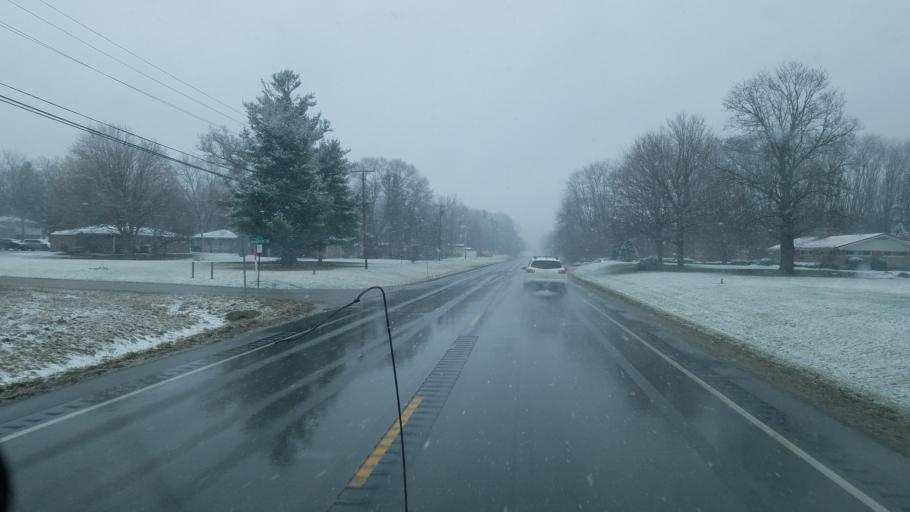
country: US
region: Indiana
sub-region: Grant County
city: Marion
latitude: 40.6104
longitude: -85.6920
